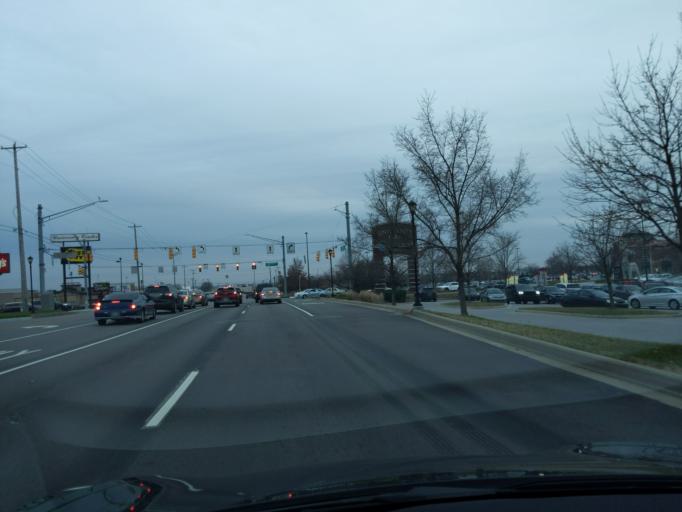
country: US
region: Indiana
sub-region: Saint Joseph County
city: Georgetown
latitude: 41.7201
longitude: -86.1879
